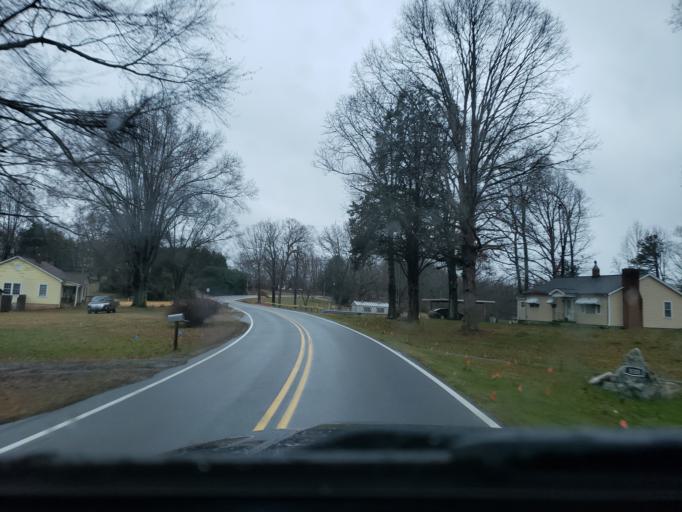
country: US
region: North Carolina
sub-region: Cleveland County
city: White Plains
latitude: 35.1894
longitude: -81.3785
